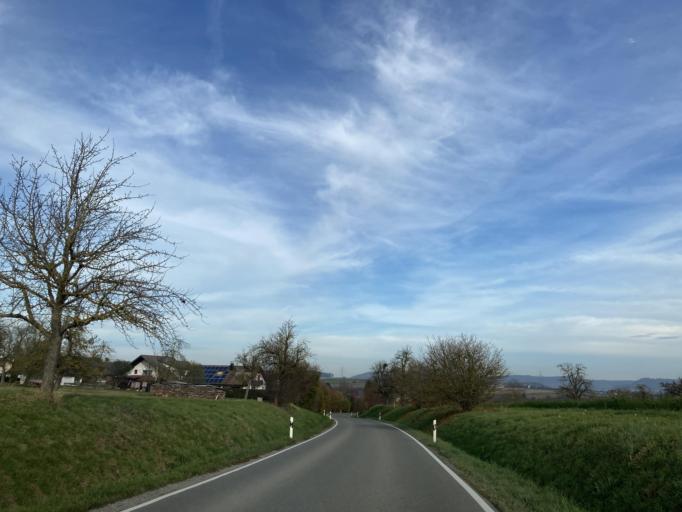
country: DE
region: Baden-Wuerttemberg
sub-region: Tuebingen Region
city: Hirrlingen
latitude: 48.4065
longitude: 8.8613
